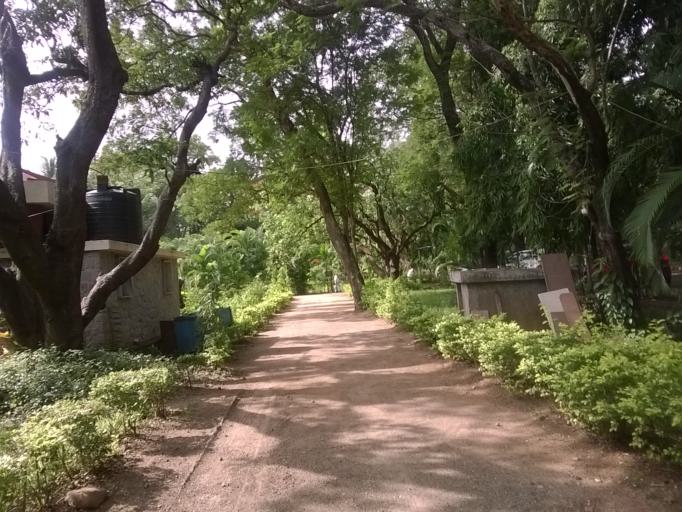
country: IN
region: Maharashtra
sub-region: Mumbai Suburban
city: Borivli
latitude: 19.2296
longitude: 72.8675
